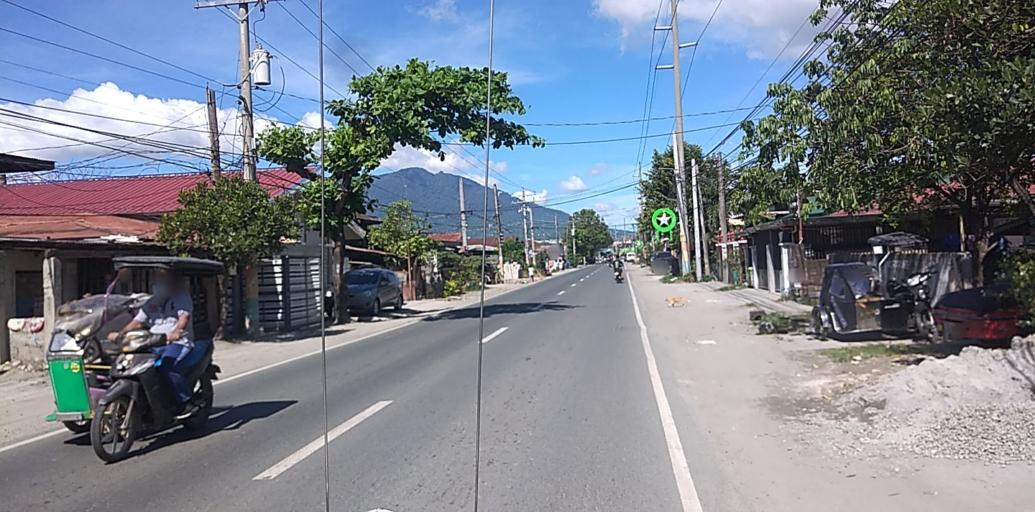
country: PH
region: Central Luzon
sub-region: Province of Pampanga
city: Arayat
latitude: 15.1318
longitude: 120.7747
